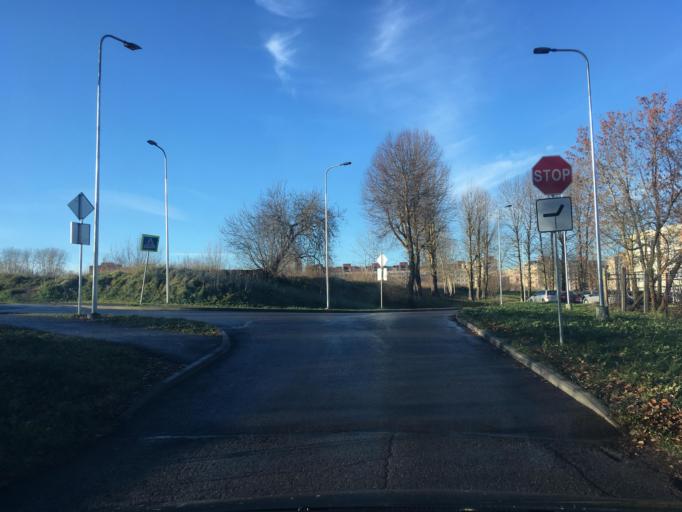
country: EE
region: Ida-Virumaa
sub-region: Narva linn
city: Narva
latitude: 59.3838
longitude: 28.1719
